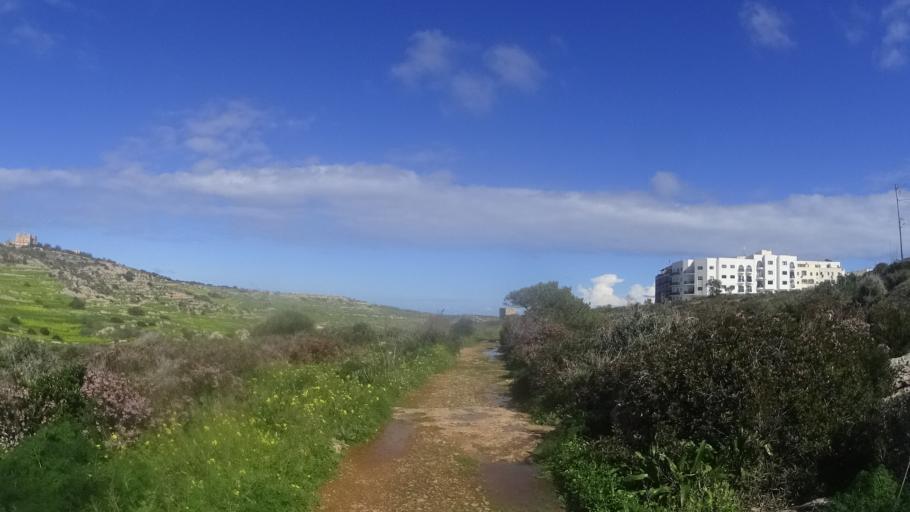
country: MT
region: Il-Mellieha
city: Mellieha
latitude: 35.9517
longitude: 14.3816
